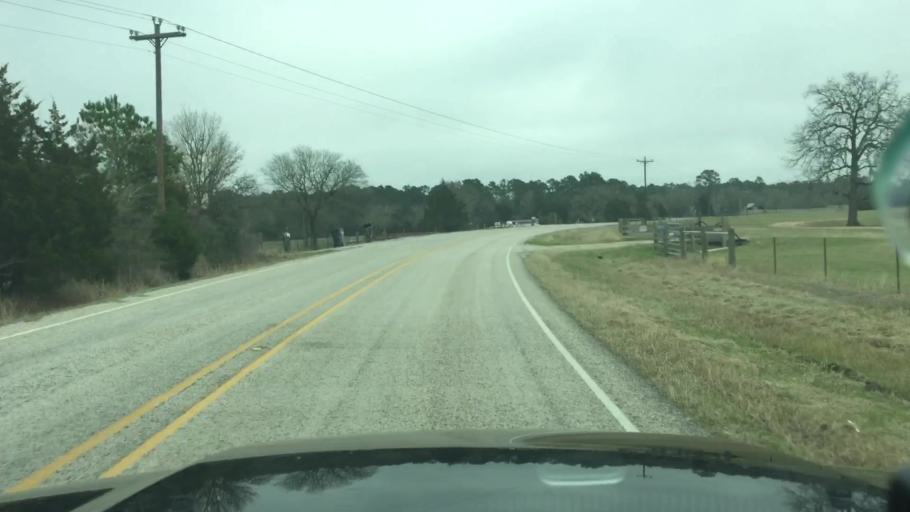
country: US
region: Texas
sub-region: Fayette County
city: La Grange
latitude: 30.0130
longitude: -96.9315
